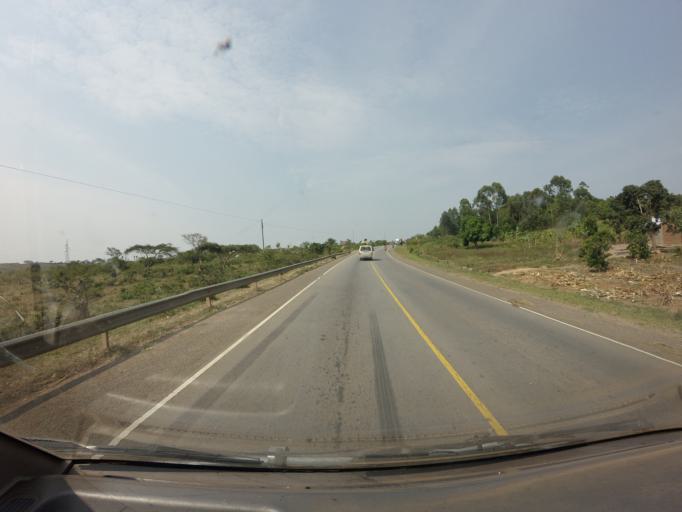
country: UG
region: Central Region
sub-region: Lwengo District
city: Lwengo
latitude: -0.3984
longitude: 31.3980
